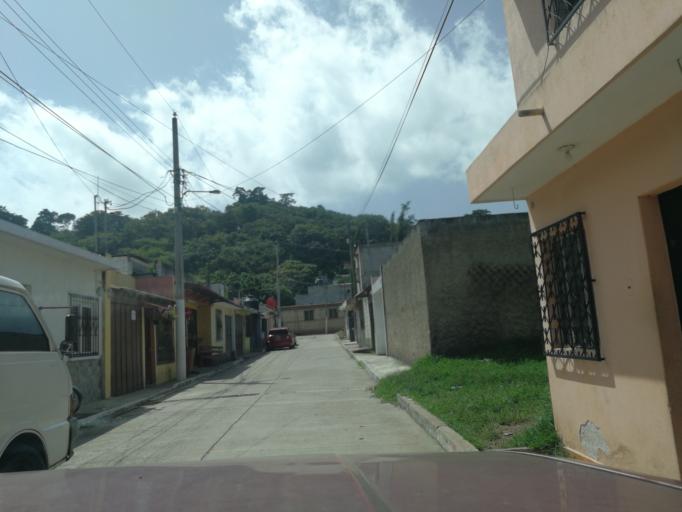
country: GT
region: Guatemala
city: Santa Catarina Pinula
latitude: 14.5476
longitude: -90.5185
